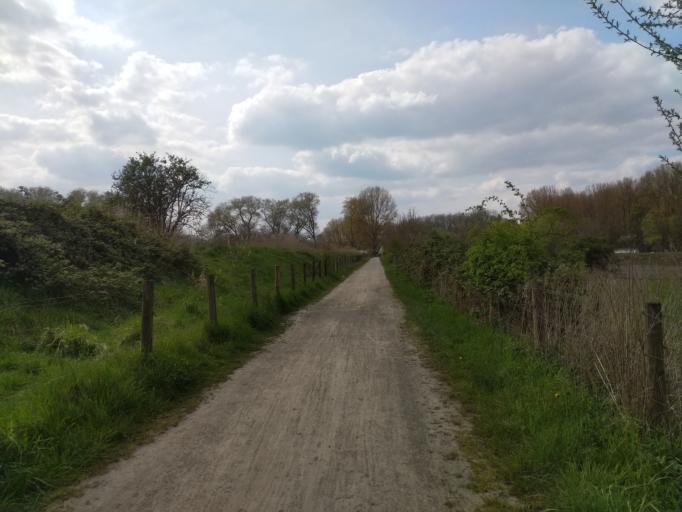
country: DE
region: North Rhine-Westphalia
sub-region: Regierungsbezirk Arnsberg
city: Hamm
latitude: 51.6822
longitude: 7.7736
